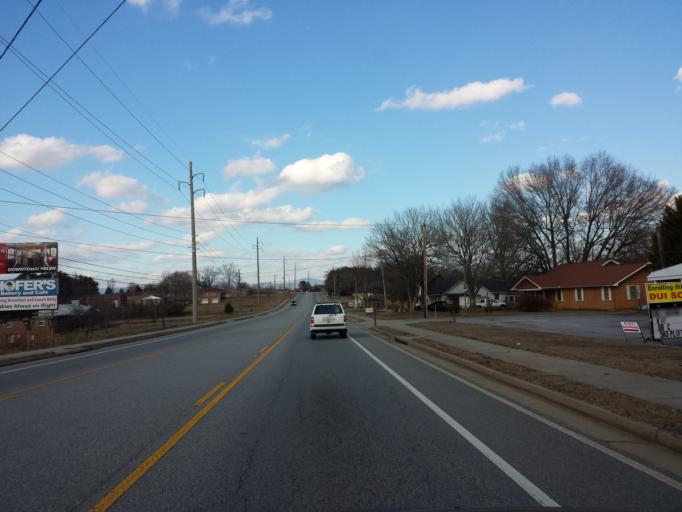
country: US
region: Georgia
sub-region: White County
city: Cleveland
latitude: 34.6230
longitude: -83.7535
